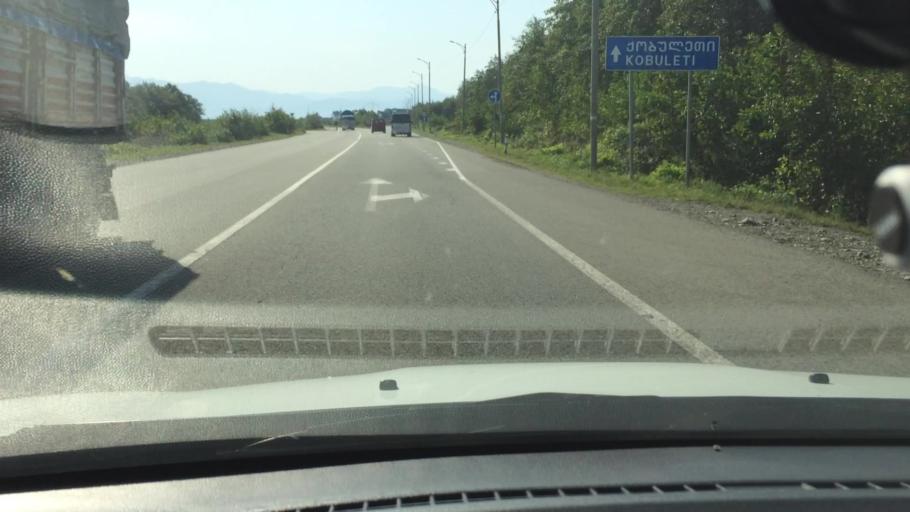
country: GE
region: Guria
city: Urek'i
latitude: 41.9256
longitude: 41.7733
